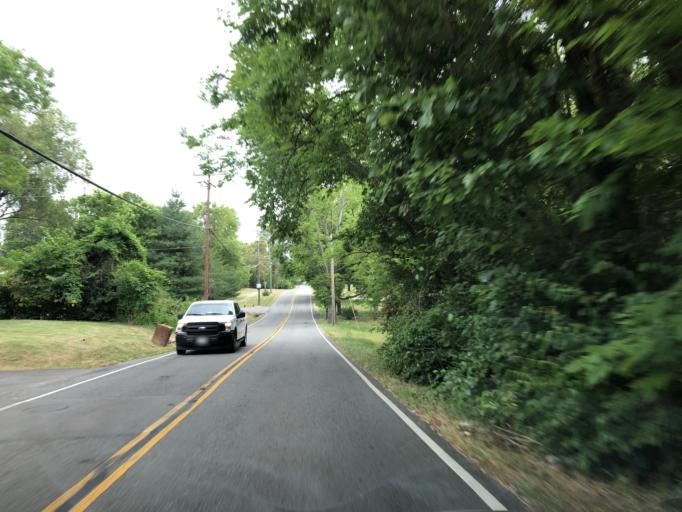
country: US
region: Tennessee
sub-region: Davidson County
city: Goodlettsville
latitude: 36.2907
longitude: -86.7430
